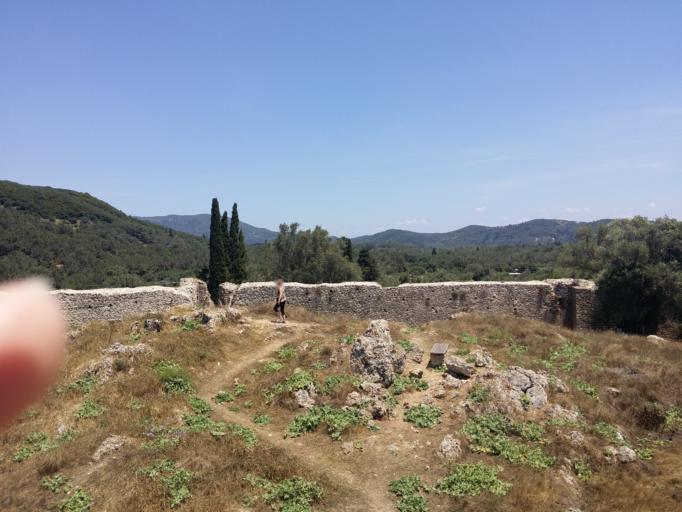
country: GR
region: Ionian Islands
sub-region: Nomos Kerkyras
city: Agios Matthaios
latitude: 39.4765
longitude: 19.8848
